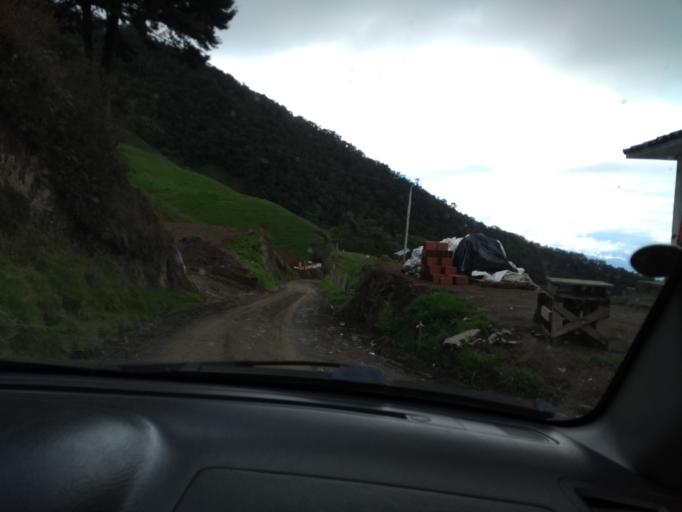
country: CO
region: Caldas
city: Salamina
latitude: 5.3799
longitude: -75.4128
